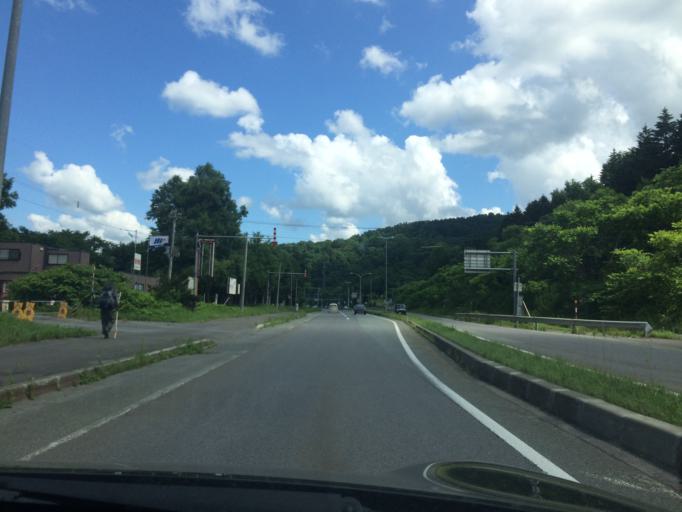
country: JP
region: Hokkaido
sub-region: Asahikawa-shi
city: Asahikawa
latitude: 43.7281
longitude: 142.2069
